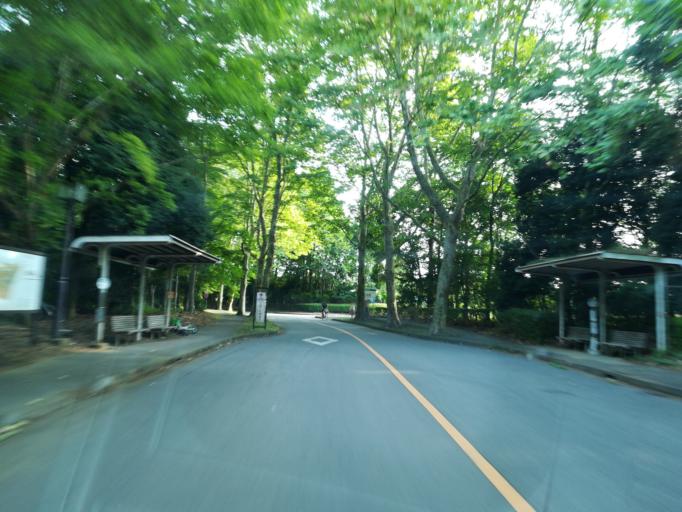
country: JP
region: Ibaraki
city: Tsukuba
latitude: 36.1187
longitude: 140.0962
